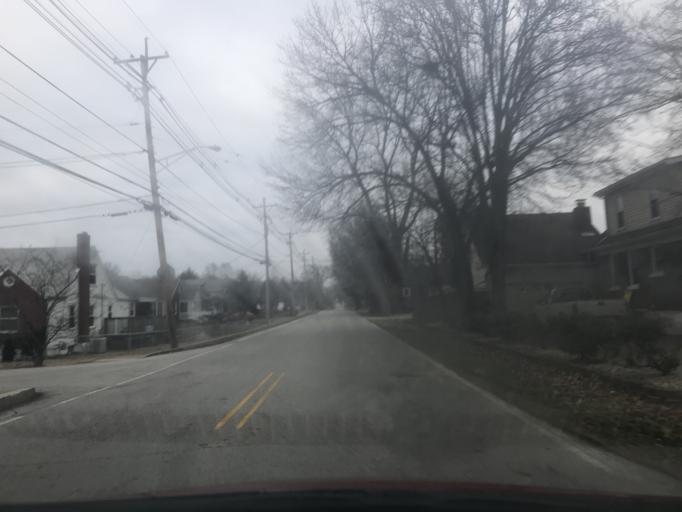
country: US
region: Kentucky
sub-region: Jefferson County
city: Audubon Park
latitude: 38.2093
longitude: -85.7267
